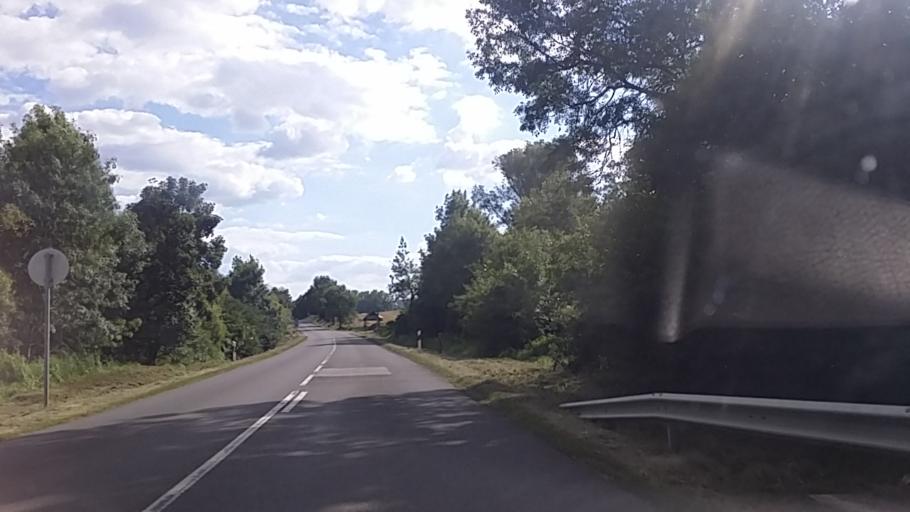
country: HU
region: Baranya
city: Sasd
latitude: 46.2800
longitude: 18.1091
